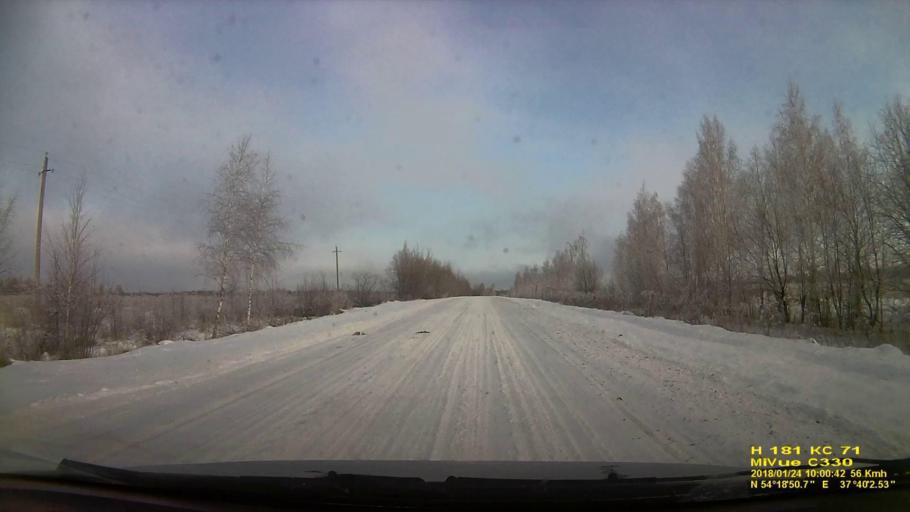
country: RU
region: Tula
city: Revyakino
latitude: 54.3141
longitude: 37.6674
